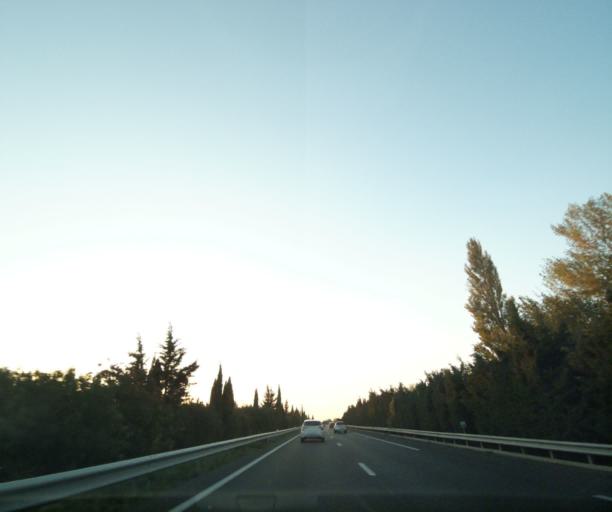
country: FR
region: Provence-Alpes-Cote d'Azur
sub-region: Departement des Bouches-du-Rhone
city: Mouries
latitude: 43.6389
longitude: 4.8898
